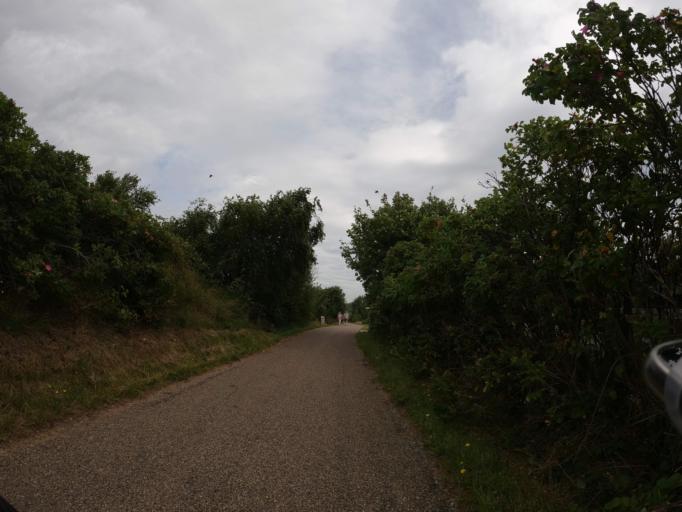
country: DE
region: Schleswig-Holstein
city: Westerland
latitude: 54.9270
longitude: 8.3250
